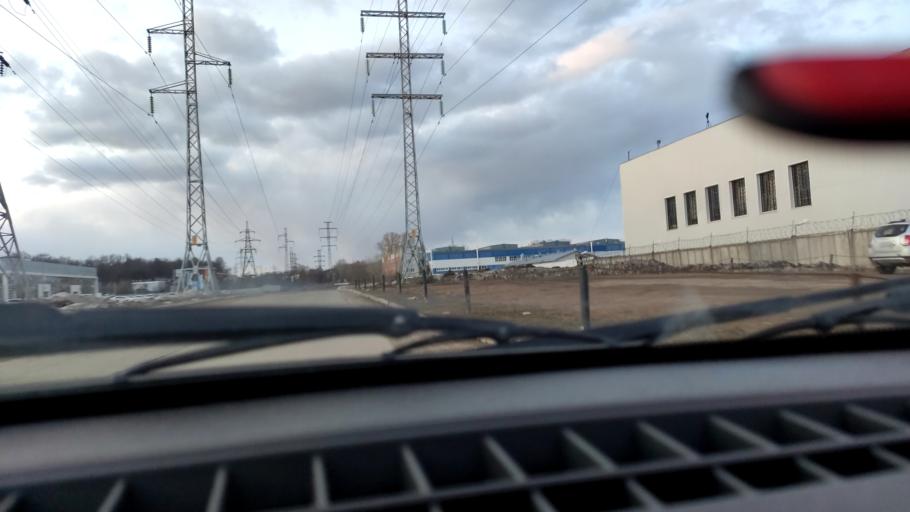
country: RU
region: Bashkortostan
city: Ufa
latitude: 54.7997
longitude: 56.0604
